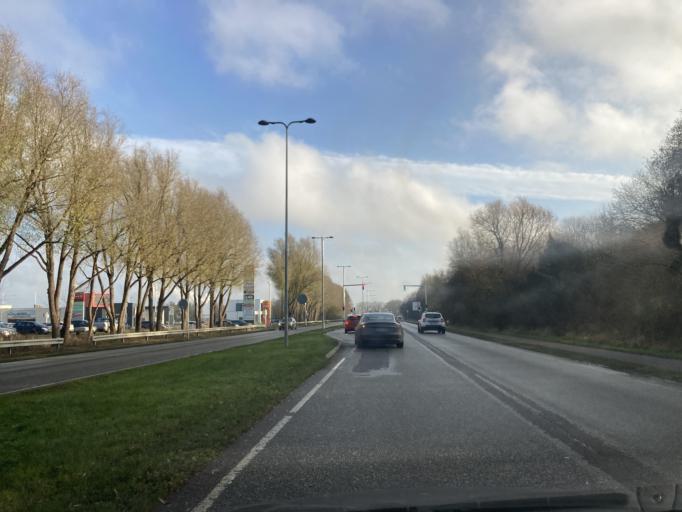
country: DK
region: Zealand
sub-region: Guldborgsund Kommune
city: Nykobing Falster
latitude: 54.7579
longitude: 11.8493
